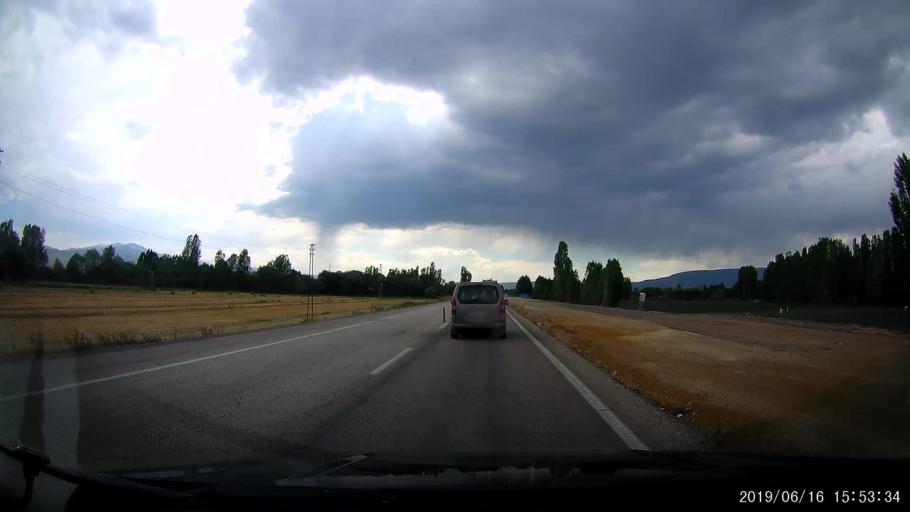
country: TR
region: Erzurum
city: Pasinler
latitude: 39.9775
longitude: 41.6454
